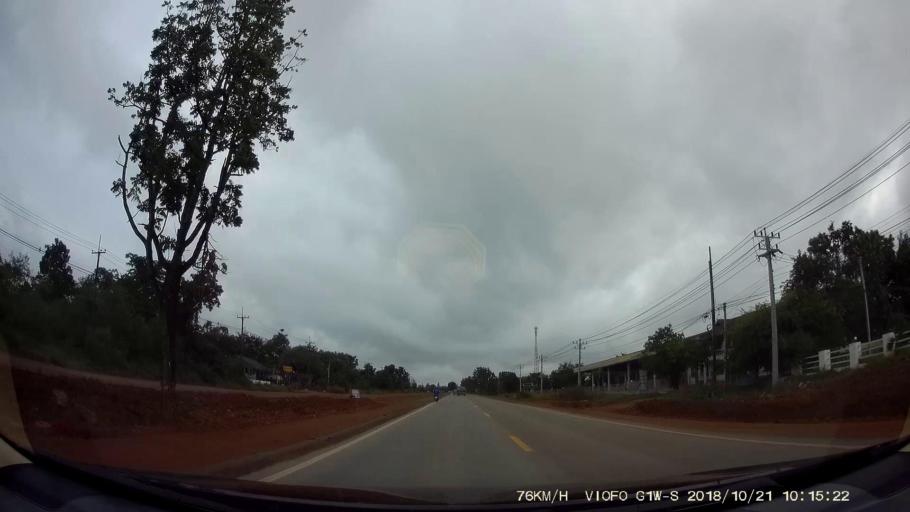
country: TH
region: Chaiyaphum
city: Phu Khiao
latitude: 16.3417
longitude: 102.1647
